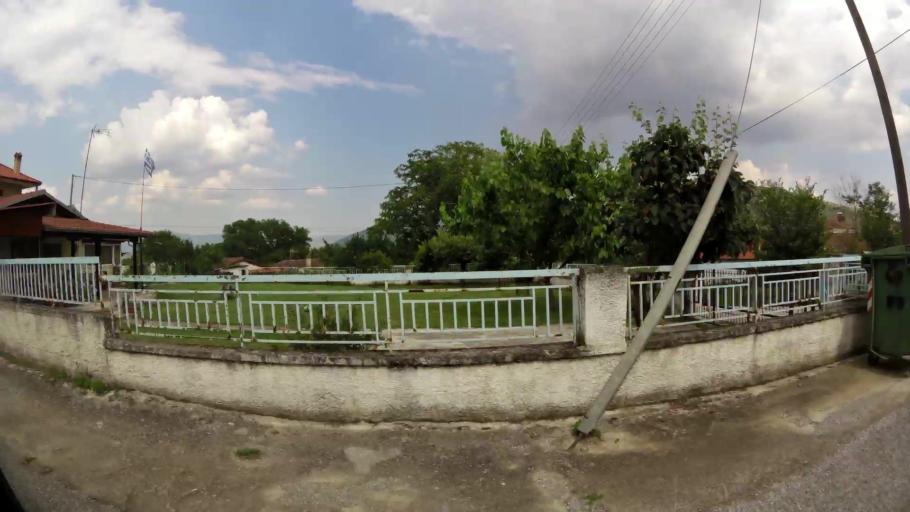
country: GR
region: West Macedonia
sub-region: Nomos Kozanis
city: Koila
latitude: 40.3475
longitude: 21.8222
